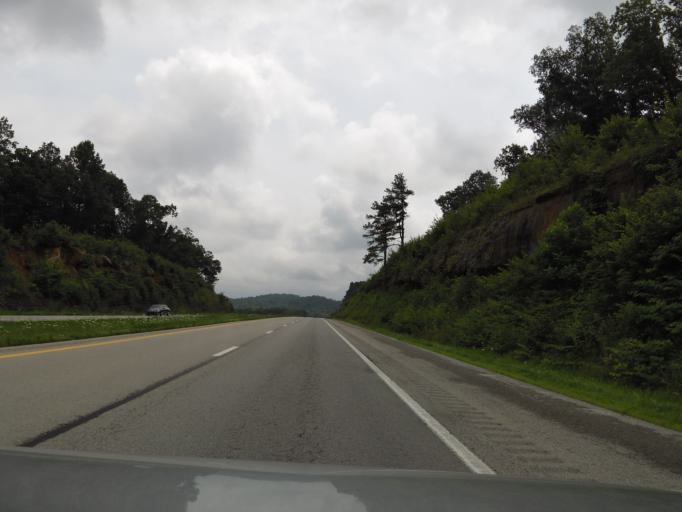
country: US
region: Kentucky
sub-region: Ohio County
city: Oak Grove
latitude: 37.3877
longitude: -86.6855
